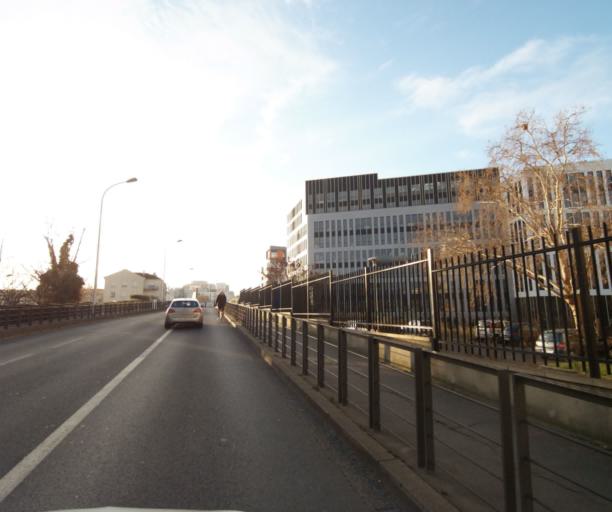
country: FR
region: Ile-de-France
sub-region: Departement des Hauts-de-Seine
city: Courbevoie
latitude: 48.9067
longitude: 2.2660
